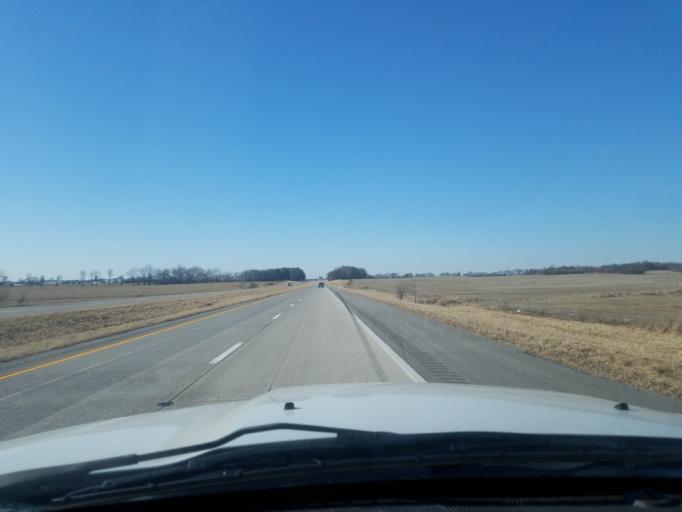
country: US
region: Kentucky
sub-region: Henderson County
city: Henderson
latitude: 37.8040
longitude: -87.5254
